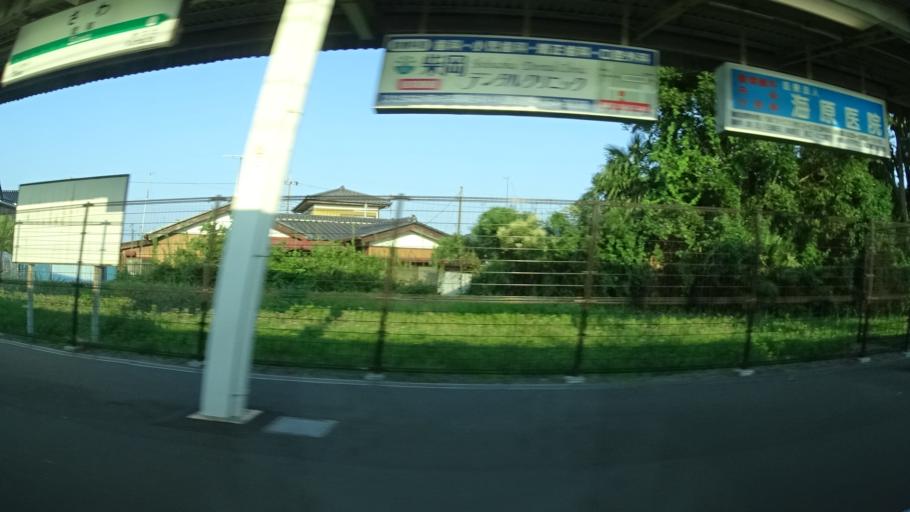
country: JP
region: Ibaraki
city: Hitachi-Naka
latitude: 36.4301
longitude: 140.5404
